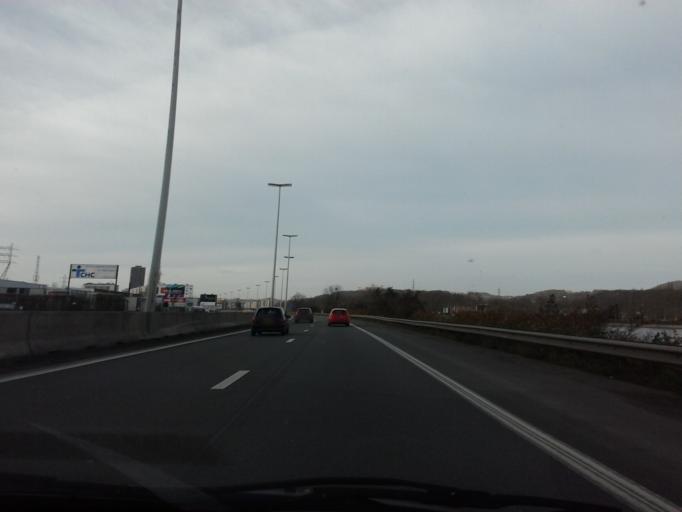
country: BE
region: Wallonia
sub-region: Province de Liege
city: Herstal
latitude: 50.6516
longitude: 5.6198
